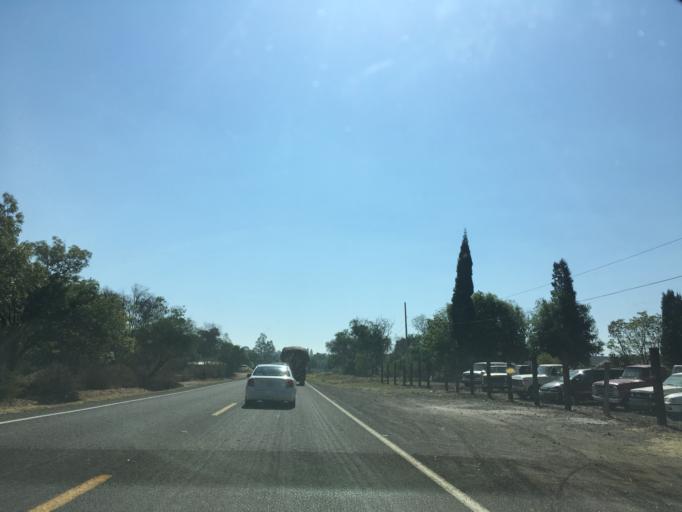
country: MX
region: Michoacan
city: Indaparapeo
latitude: 19.7872
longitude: -100.9841
